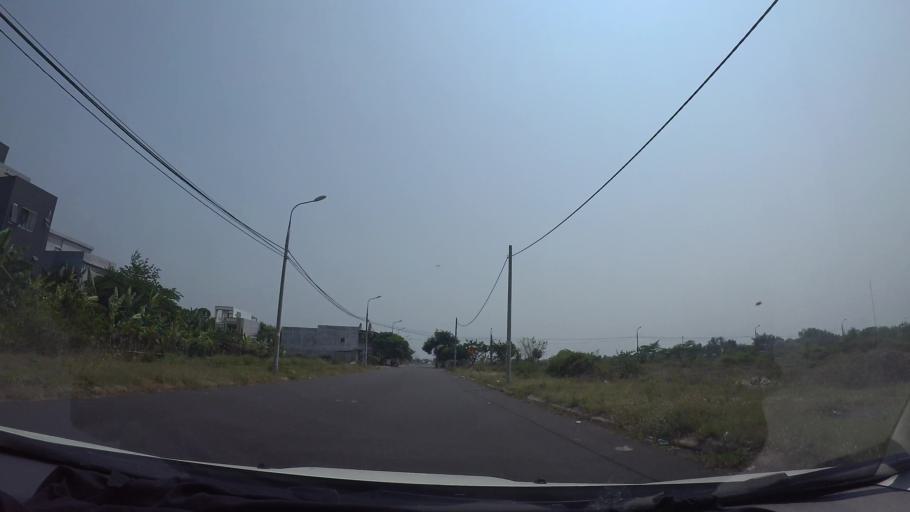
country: VN
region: Da Nang
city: Cam Le
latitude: 15.9801
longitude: 108.2115
